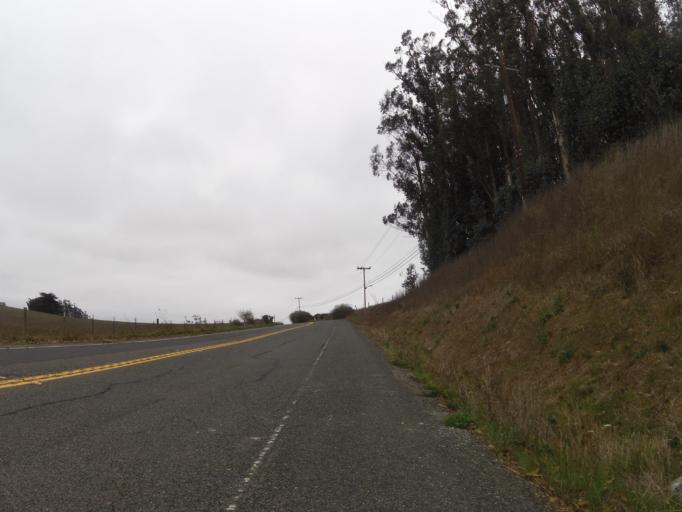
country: US
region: California
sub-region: Sonoma County
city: Occidental
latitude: 38.2598
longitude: -122.9022
